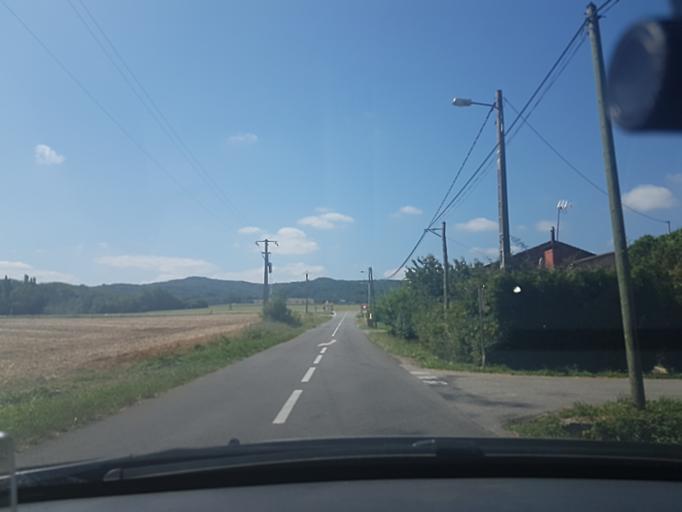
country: FR
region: Midi-Pyrenees
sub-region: Departement de l'Ariege
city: Mirepoix
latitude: 43.0784
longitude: 1.7737
